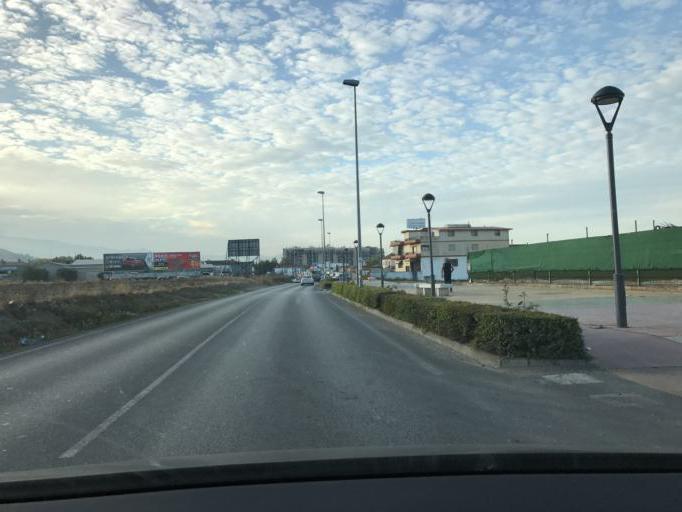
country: ES
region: Andalusia
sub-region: Provincia de Granada
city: Pulianas
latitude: 37.2168
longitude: -3.6096
